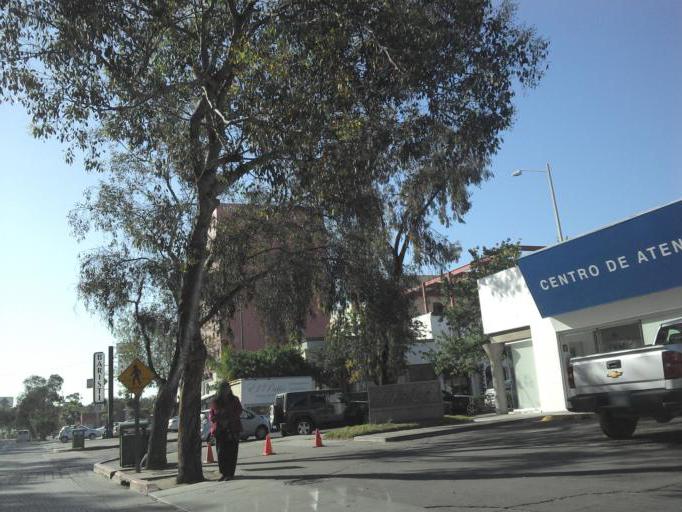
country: MX
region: Baja California
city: Tijuana
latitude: 32.5194
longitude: -117.0087
